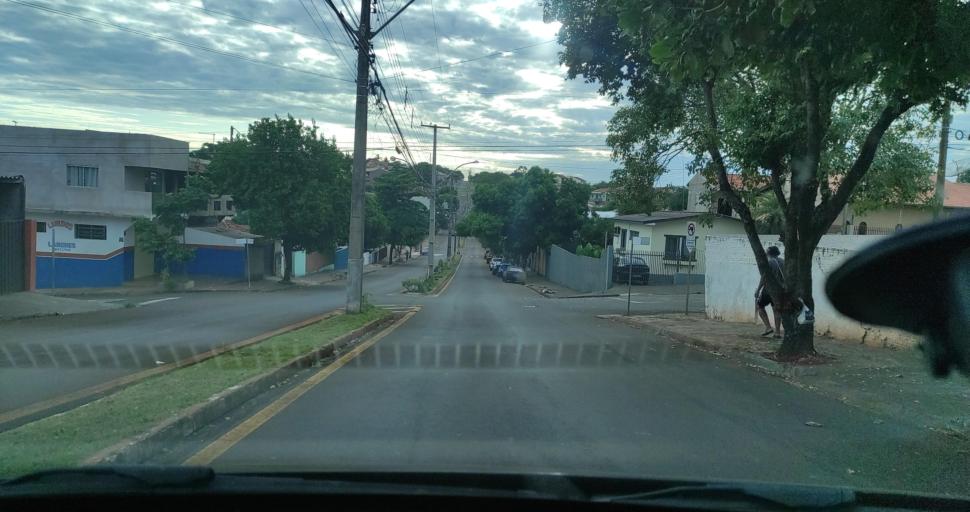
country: BR
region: Parana
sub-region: Ibipora
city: Ibipora
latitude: -23.2671
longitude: -51.0435
